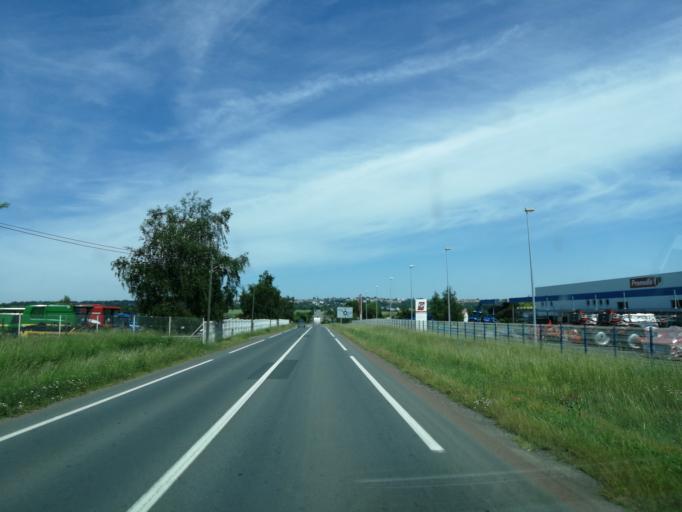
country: FR
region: Pays de la Loire
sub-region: Departement de la Vendee
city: Antigny
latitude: 46.6244
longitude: -0.7747
